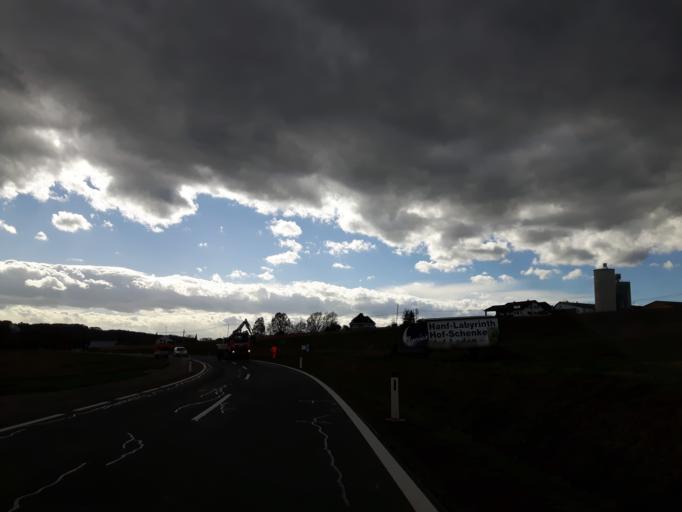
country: AT
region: Styria
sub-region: Politischer Bezirk Suedoststeiermark
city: Schwarzau im Schwarzautal
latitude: 46.8723
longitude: 15.6556
